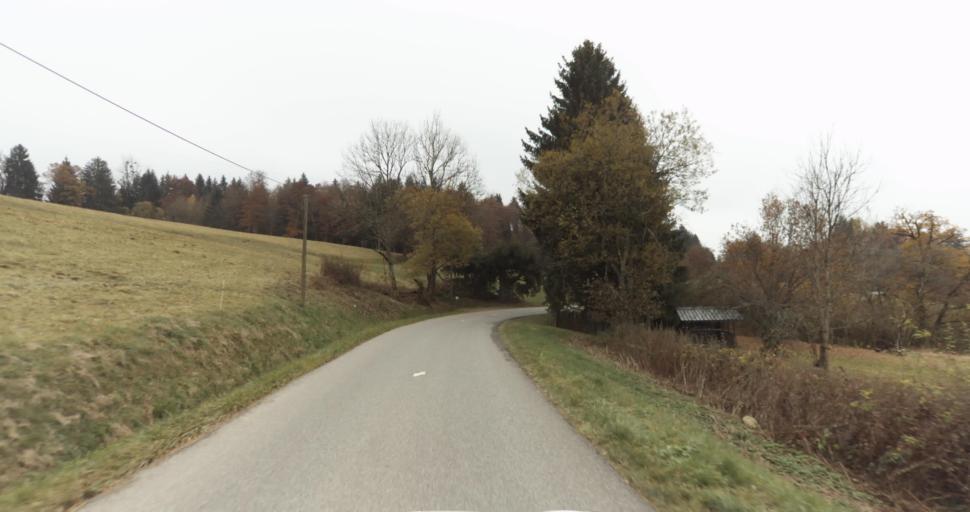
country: FR
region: Rhone-Alpes
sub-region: Departement de la Haute-Savoie
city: Saint-Jorioz
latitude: 45.7695
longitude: 6.1331
